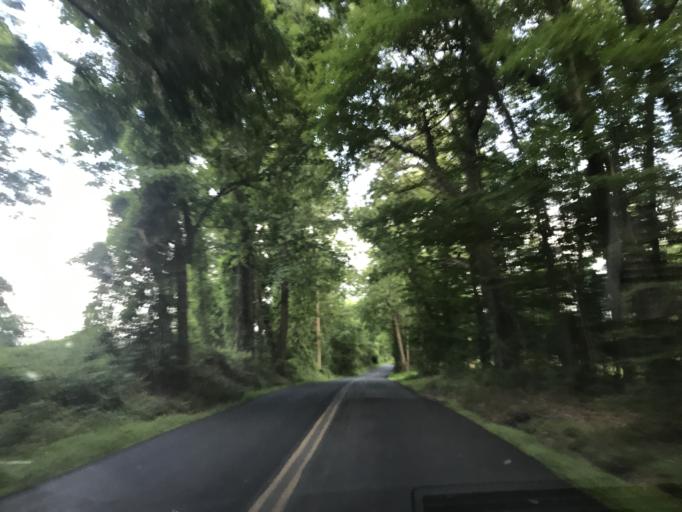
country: US
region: Maryland
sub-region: Harford County
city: Aberdeen
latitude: 39.5191
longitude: -76.2087
